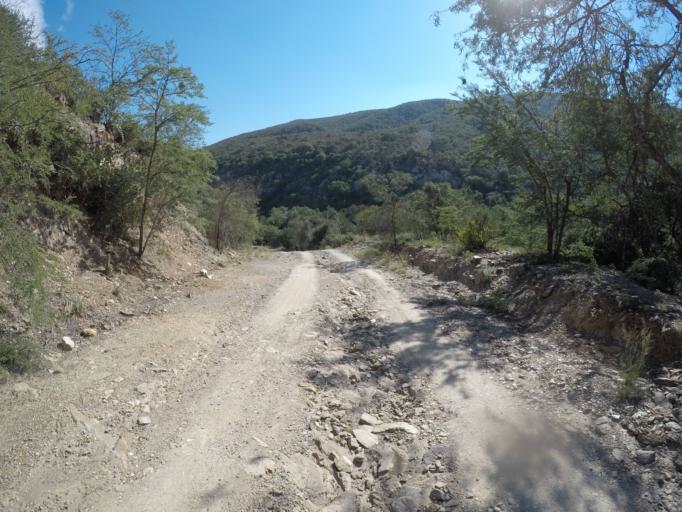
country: ZA
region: Eastern Cape
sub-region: Cacadu District Municipality
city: Kareedouw
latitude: -33.6458
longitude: 24.4529
